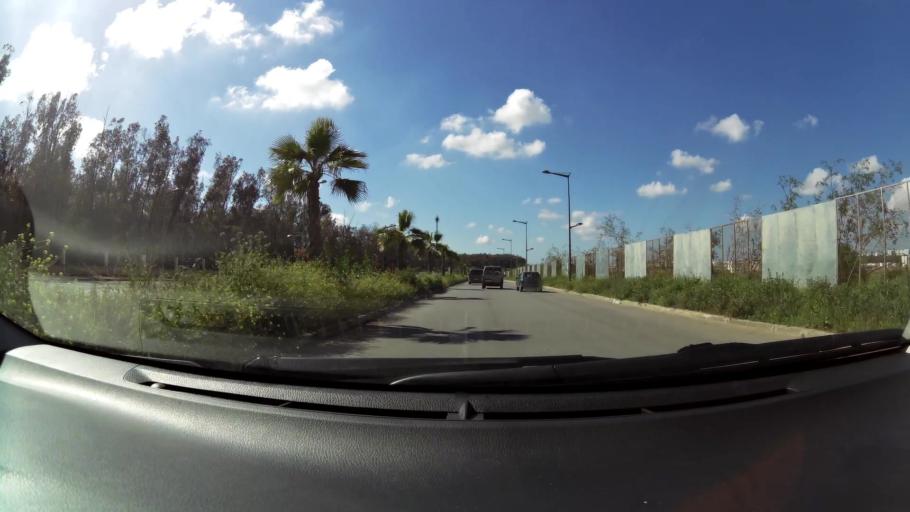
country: MA
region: Grand Casablanca
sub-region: Nouaceur
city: Bouskoura
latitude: 33.4746
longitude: -7.6180
